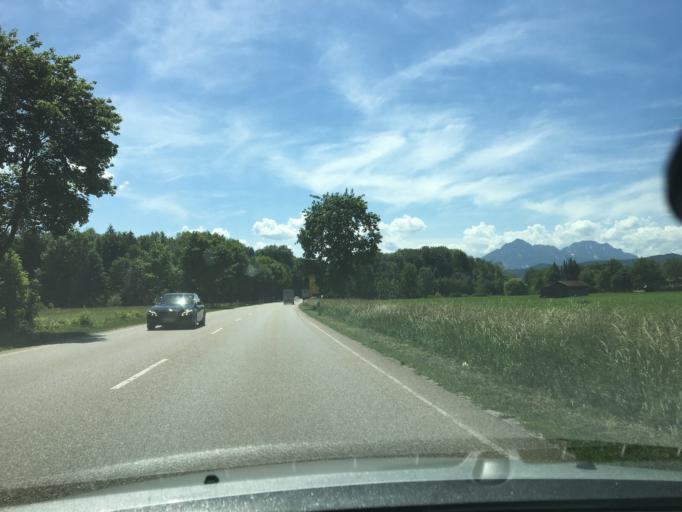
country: DE
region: Bavaria
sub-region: Upper Bavaria
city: Freilassing
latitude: 47.8444
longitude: 12.9935
